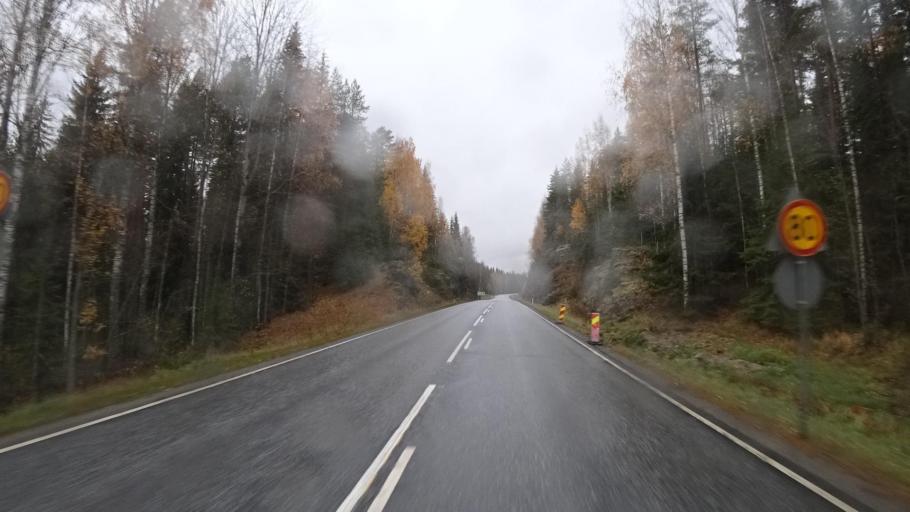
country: FI
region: Northern Savo
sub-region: Varkaus
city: Kangaslampi
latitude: 62.4700
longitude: 28.3242
